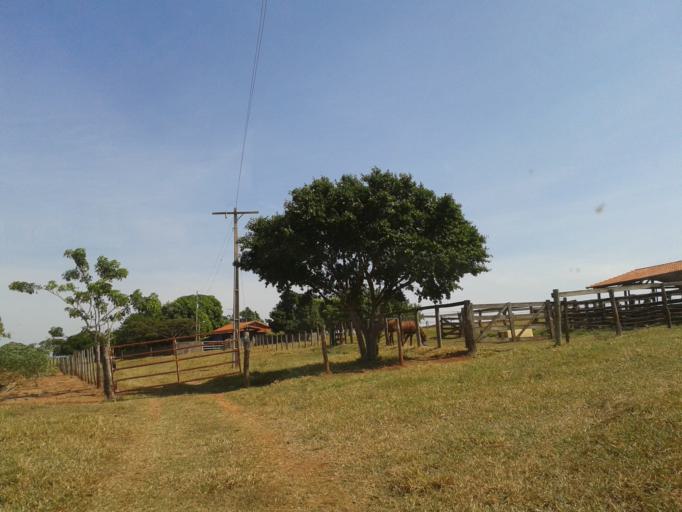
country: BR
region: Minas Gerais
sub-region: Campina Verde
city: Campina Verde
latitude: -19.4789
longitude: -49.5810
